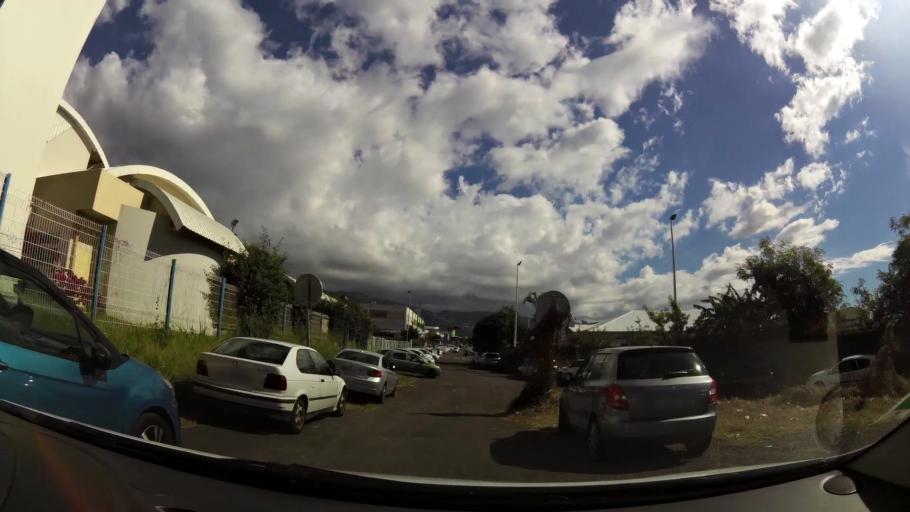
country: RE
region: Reunion
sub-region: Reunion
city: Saint-Denis
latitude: -20.8912
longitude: 55.4987
